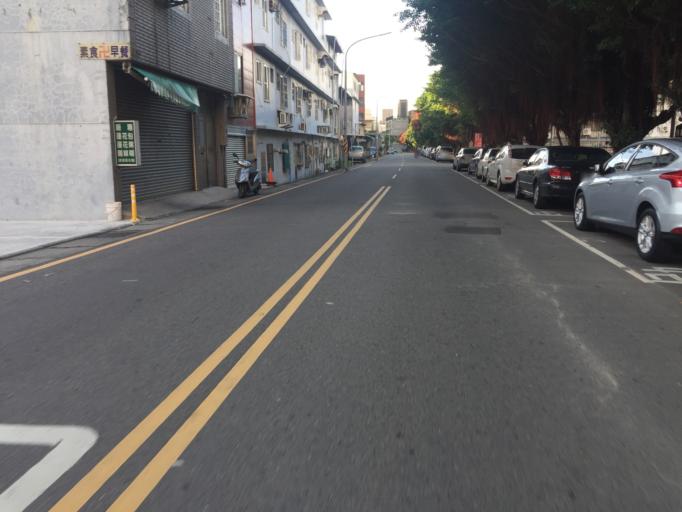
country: TW
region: Taiwan
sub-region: Hsinchu
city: Hsinchu
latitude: 24.8173
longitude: 120.9781
